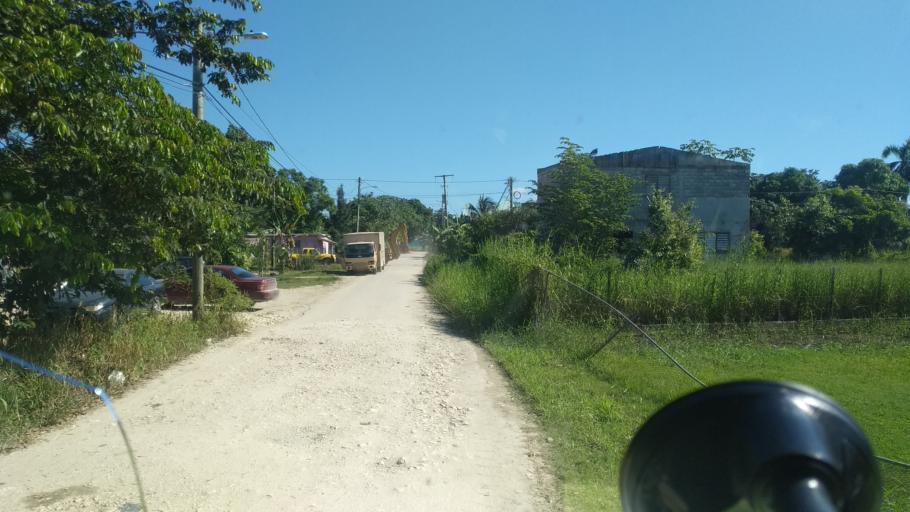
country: BZ
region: Belize
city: Belize City
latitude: 17.5551
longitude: -88.3052
